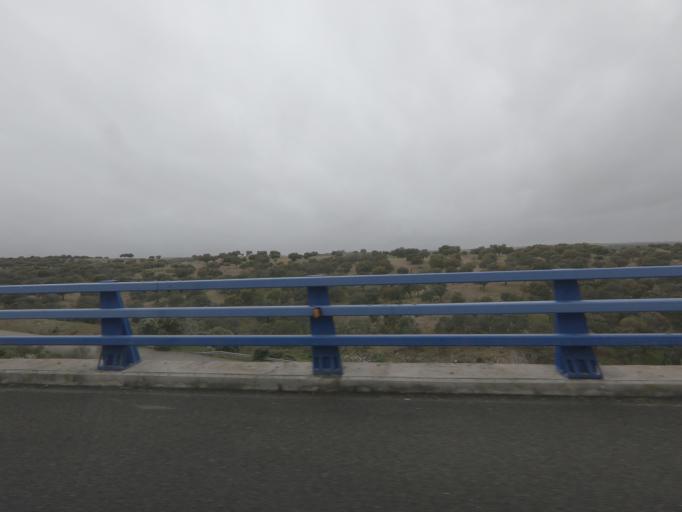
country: ES
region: Extremadura
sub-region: Provincia de Caceres
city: Casar de Caceres
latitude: 39.6018
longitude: -6.4062
